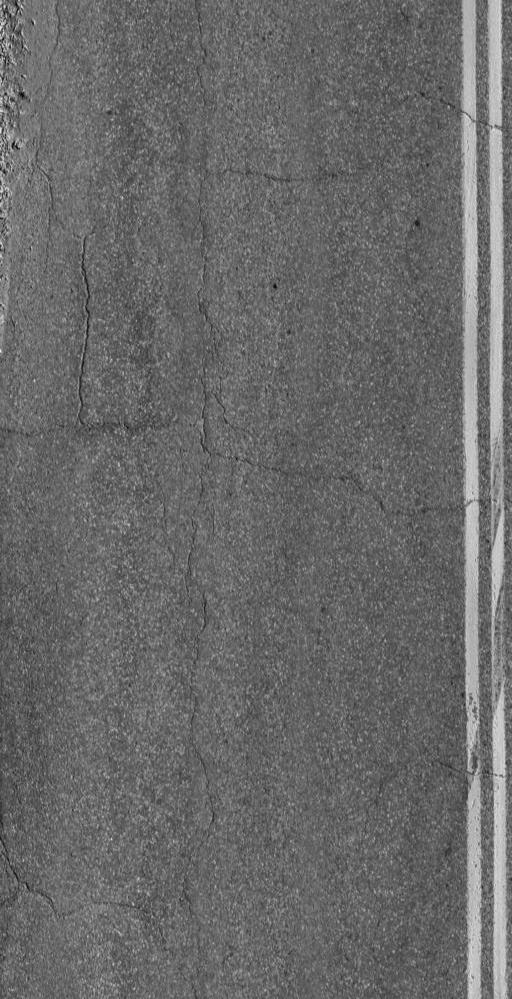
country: US
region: Vermont
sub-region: Chittenden County
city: Essex Junction
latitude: 44.5053
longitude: -73.1330
